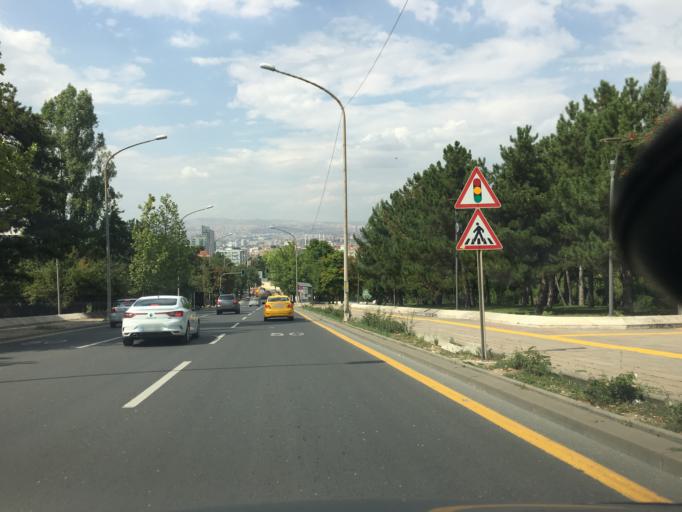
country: TR
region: Ankara
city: Cankaya
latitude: 39.8948
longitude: 32.8621
